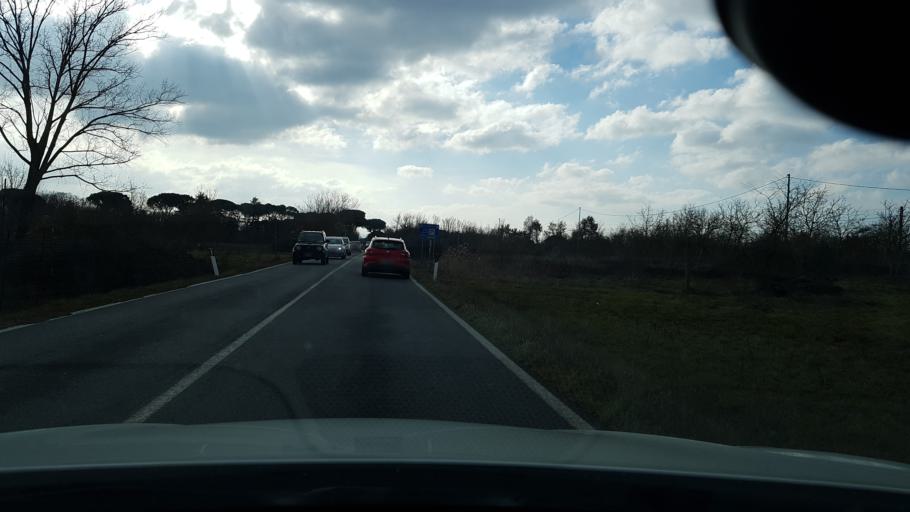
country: IT
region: Tuscany
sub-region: Province of Arezzo
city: Terontola
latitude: 43.1645
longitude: 12.0153
